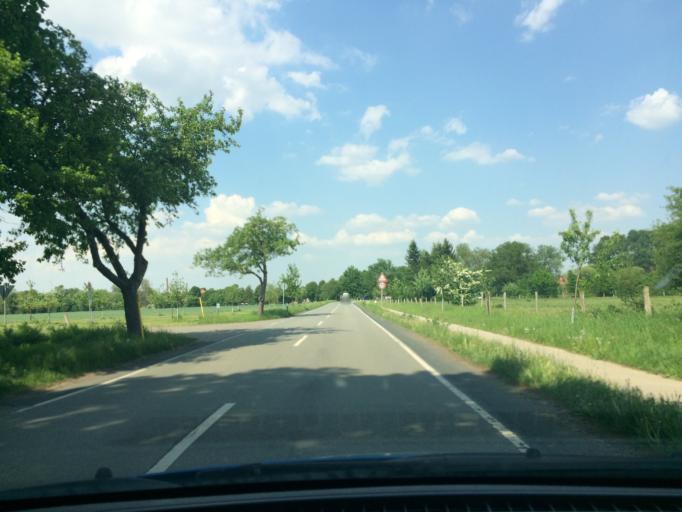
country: DE
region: Lower Saxony
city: Neu Darchau
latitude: 53.2769
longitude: 10.9274
